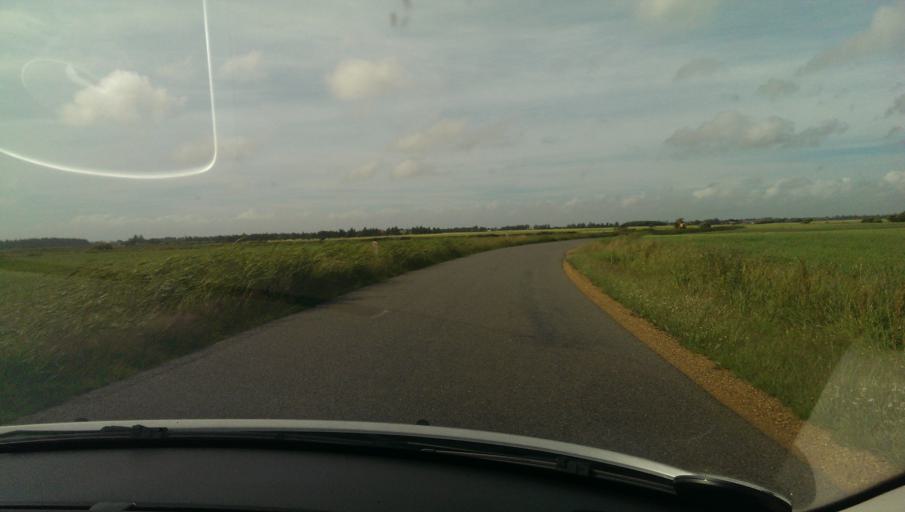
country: DK
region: Central Jutland
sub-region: Holstebro Kommune
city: Ulfborg
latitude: 56.2899
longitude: 8.2166
